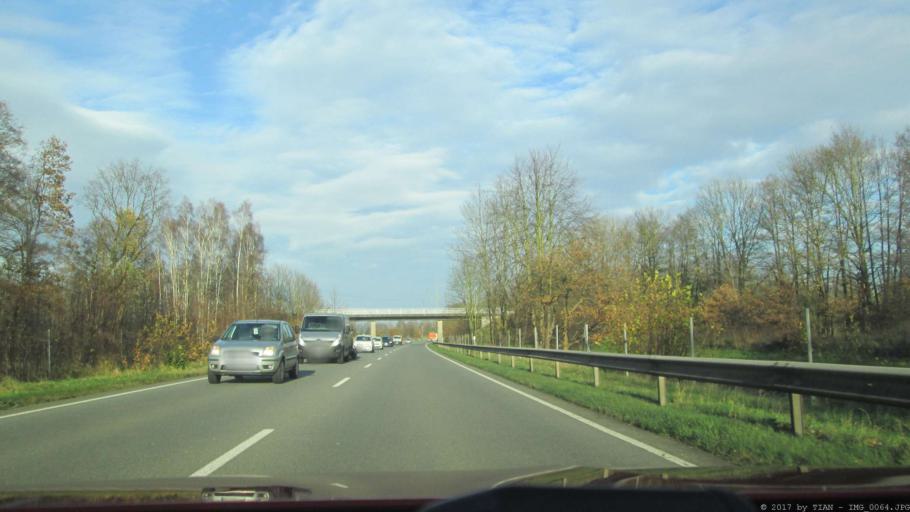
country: DE
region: Lower Saxony
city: Handorf
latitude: 53.3566
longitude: 10.3424
